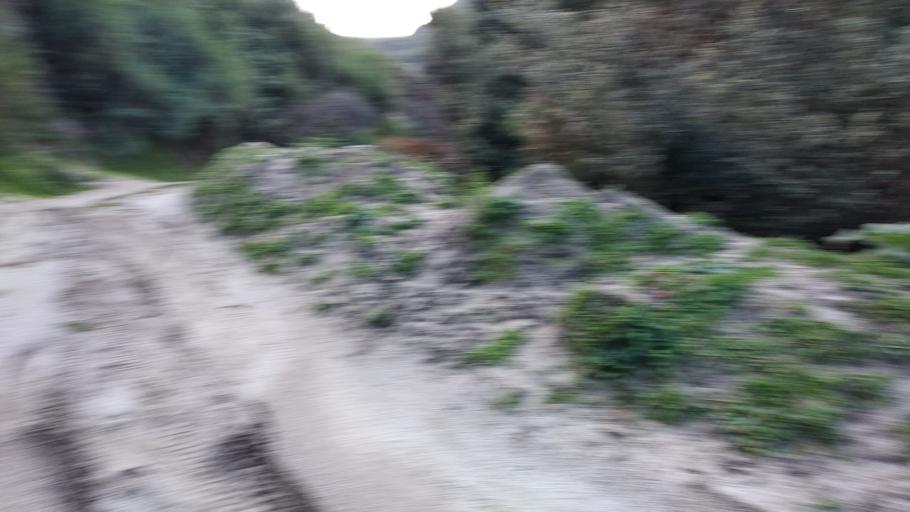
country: IT
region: Calabria
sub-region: Provincia di Reggio Calabria
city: San Roberto
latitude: 38.2348
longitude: 15.7753
